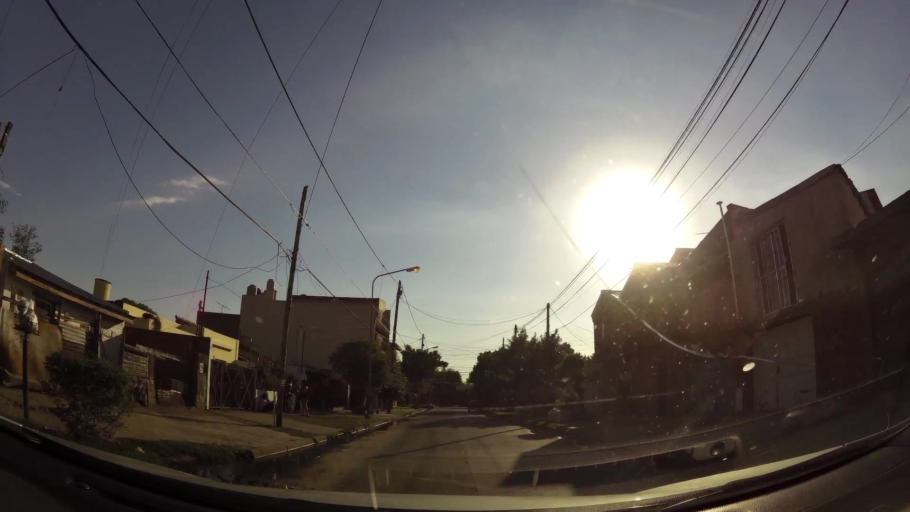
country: AR
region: Buenos Aires
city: Santa Catalina - Dique Lujan
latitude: -34.4612
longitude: -58.6636
